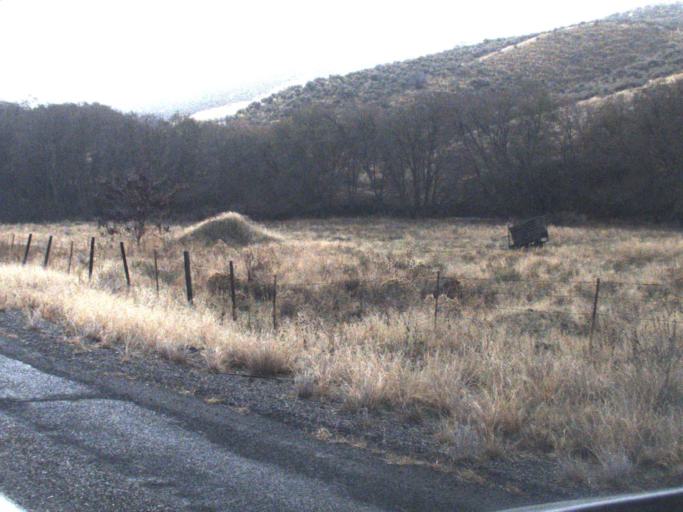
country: US
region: Washington
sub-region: Asotin County
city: Clarkston Heights-Vineland
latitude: 46.4163
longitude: -117.2759
